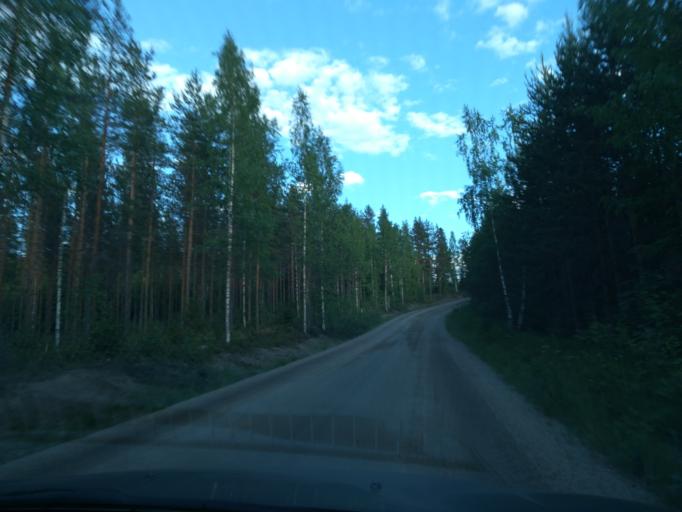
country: FI
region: Southern Savonia
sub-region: Mikkeli
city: Puumala
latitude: 61.6220
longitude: 28.1113
